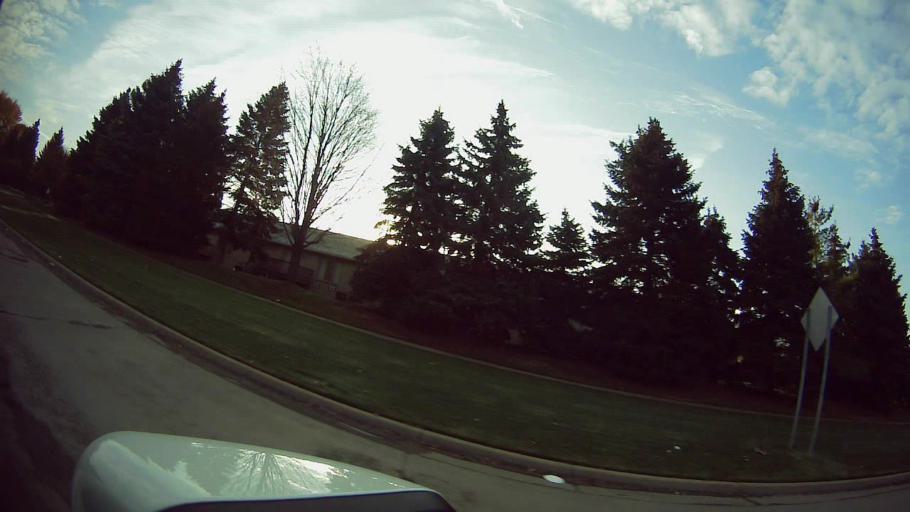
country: US
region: Michigan
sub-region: Macomb County
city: Fraser
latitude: 42.5537
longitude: -82.9776
